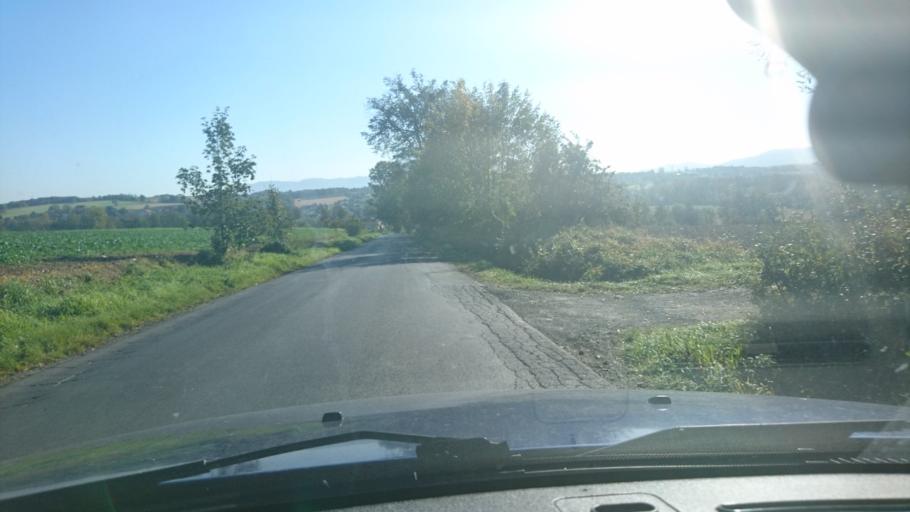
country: PL
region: Silesian Voivodeship
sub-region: Powiat bielski
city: Bronow
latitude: 49.8541
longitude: 18.9303
